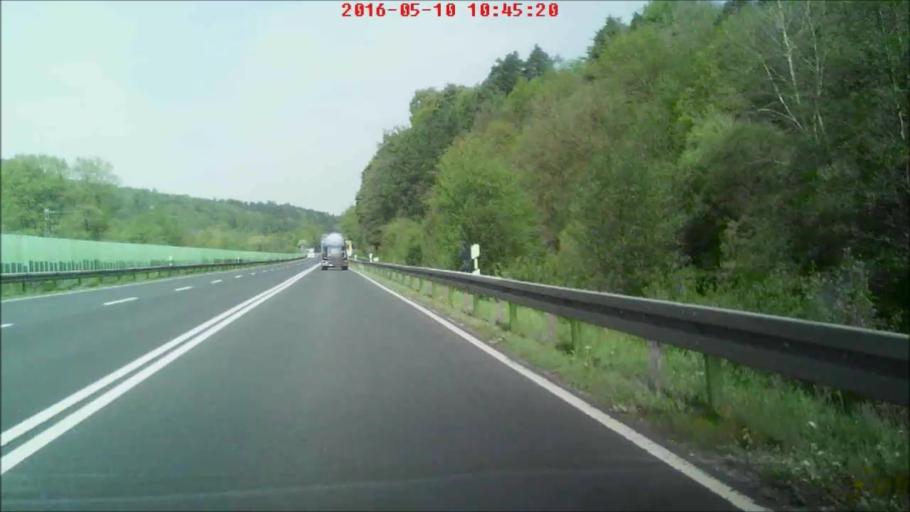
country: DE
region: Hesse
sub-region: Regierungsbezirk Kassel
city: Burghaun
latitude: 50.7307
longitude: 9.6994
